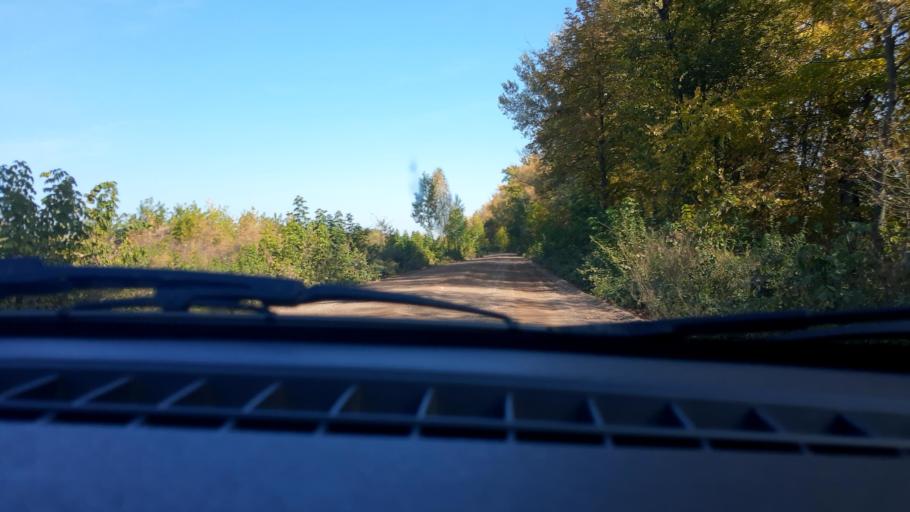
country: RU
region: Bashkortostan
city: Mikhaylovka
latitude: 54.7411
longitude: 55.8534
